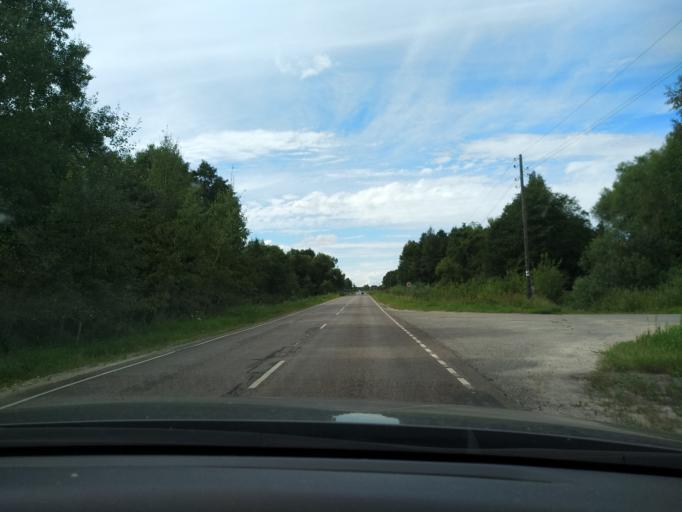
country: RU
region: Moskovskaya
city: Krasnyy Tkach
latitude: 55.3882
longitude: 39.1748
